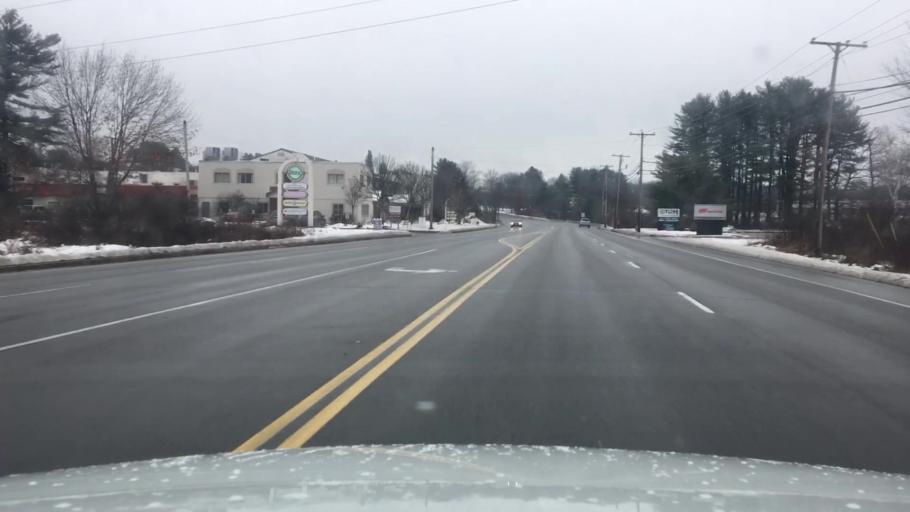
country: US
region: Maine
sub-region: Cumberland County
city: Scarborough
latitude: 43.6069
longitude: -70.3150
